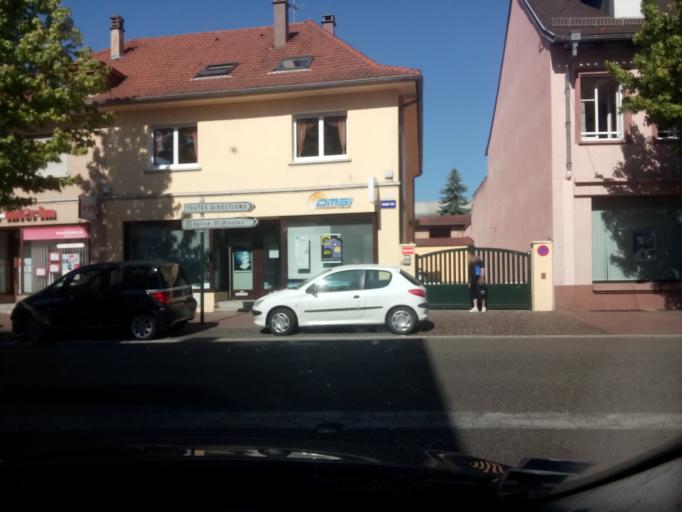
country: FR
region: Alsace
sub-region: Departement du Bas-Rhin
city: Haguenau
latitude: 48.8174
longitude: 7.7927
